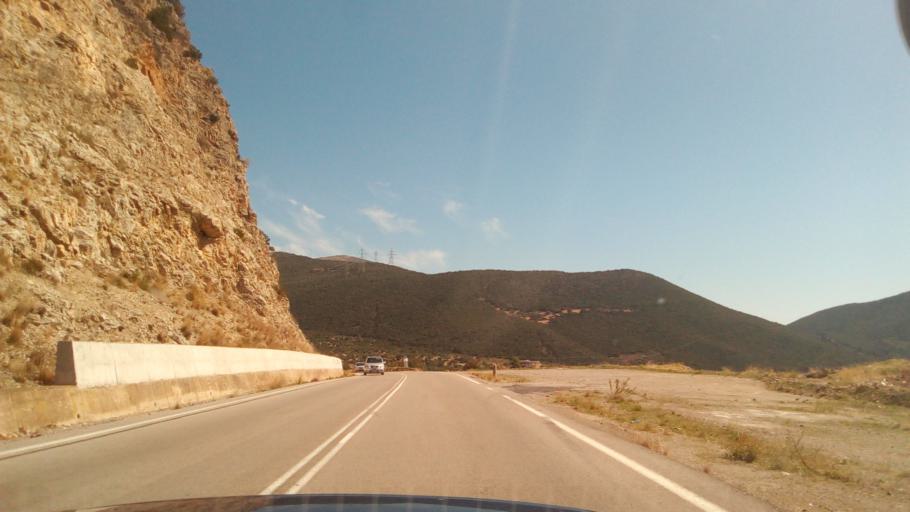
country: GR
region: West Greece
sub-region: Nomos Achaias
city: Aigio
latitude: 38.3598
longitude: 22.1317
